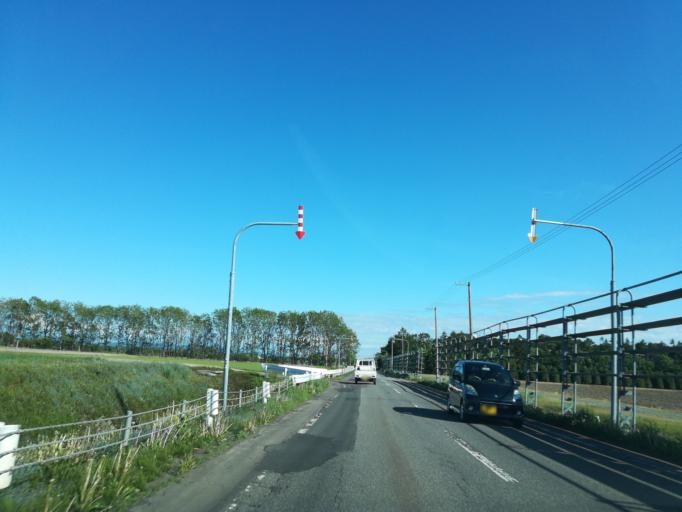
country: JP
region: Hokkaido
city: Ebetsu
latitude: 43.0739
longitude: 141.6032
